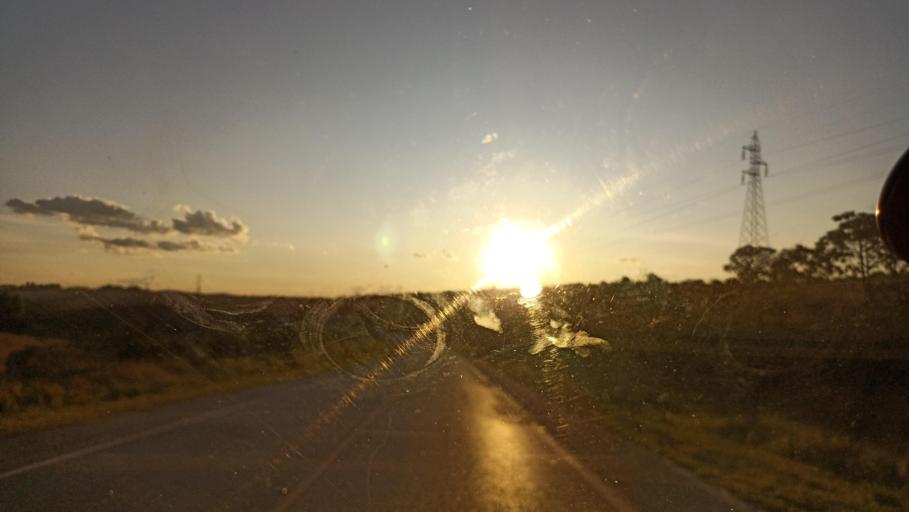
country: BR
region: Minas Gerais
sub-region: Sao Joao Del Rei
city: Sao Joao del Rei
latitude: -21.2257
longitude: -44.3706
